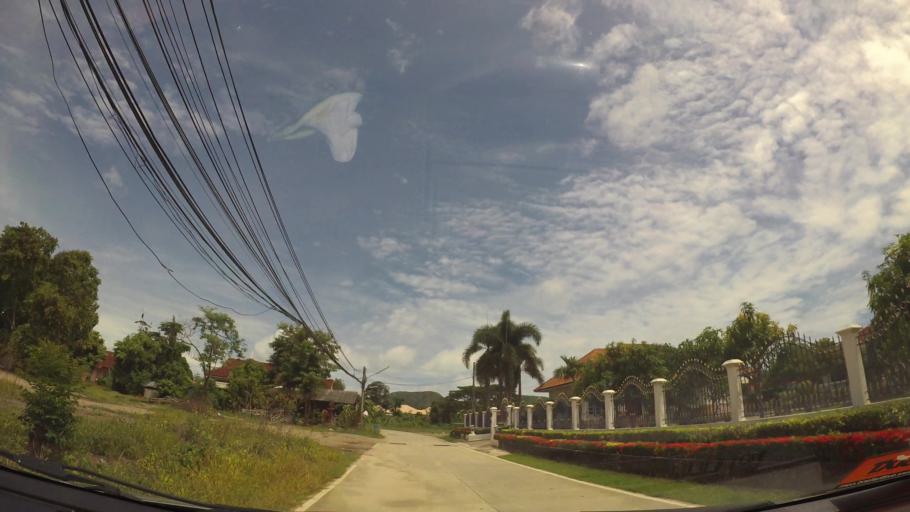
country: TH
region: Chon Buri
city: Sattahip
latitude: 12.7030
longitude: 100.8863
